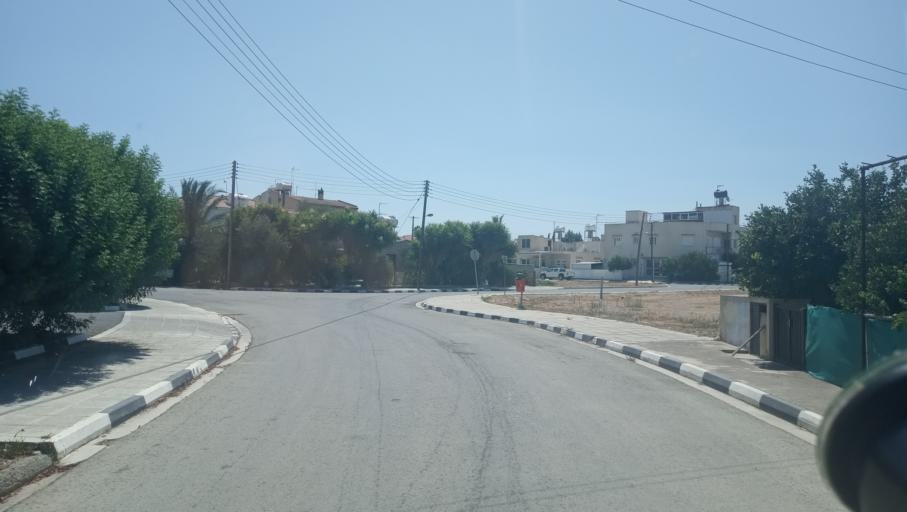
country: CY
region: Lefkosia
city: Psimolofou
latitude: 35.0619
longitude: 33.2608
